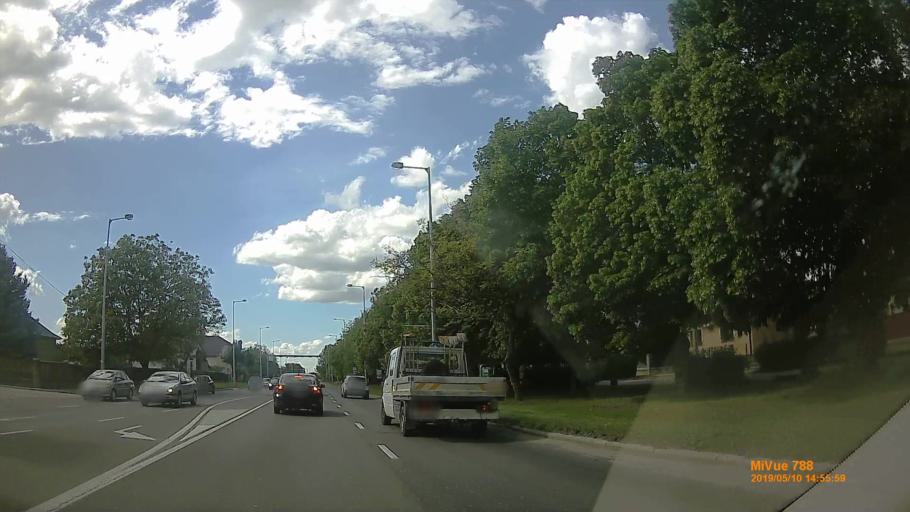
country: HU
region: Fejer
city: Szekesfehervar
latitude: 47.1974
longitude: 18.4420
